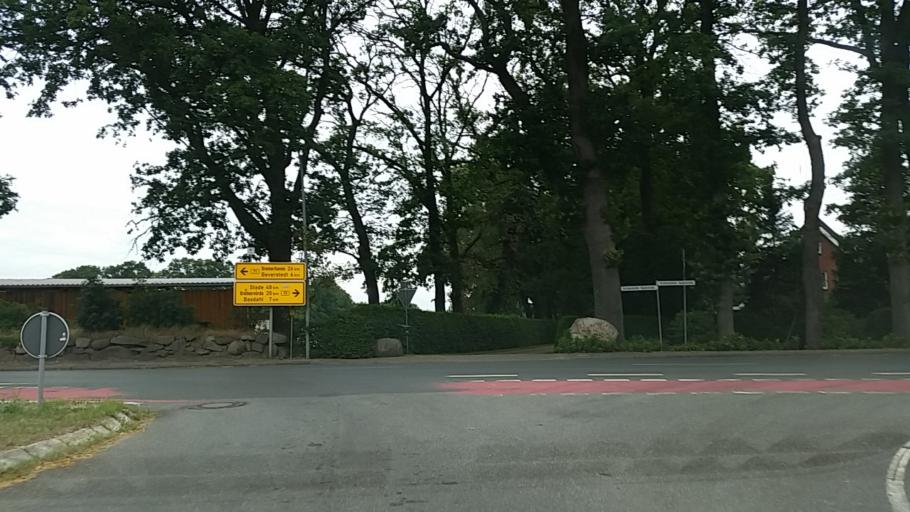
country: DE
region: Lower Saxony
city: Beverstedt
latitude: 53.4250
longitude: 8.9013
